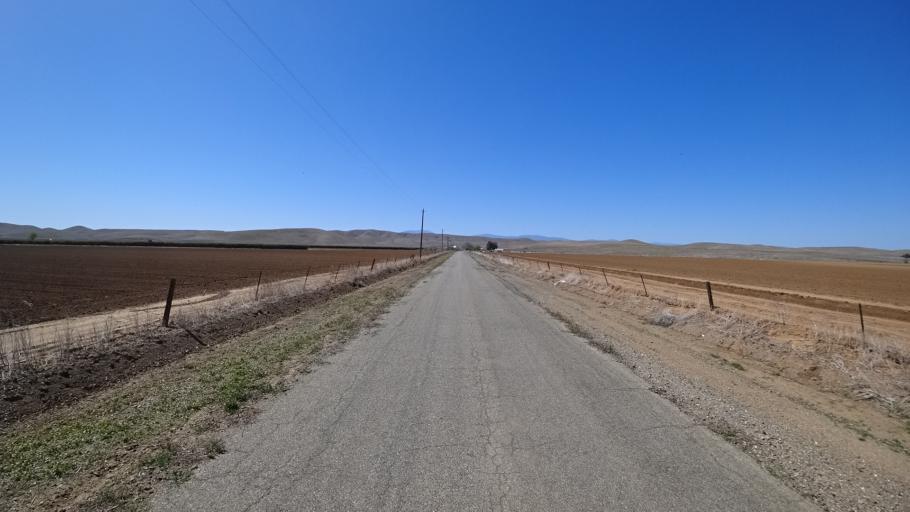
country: US
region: California
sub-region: Glenn County
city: Willows
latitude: 39.4656
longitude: -122.2901
